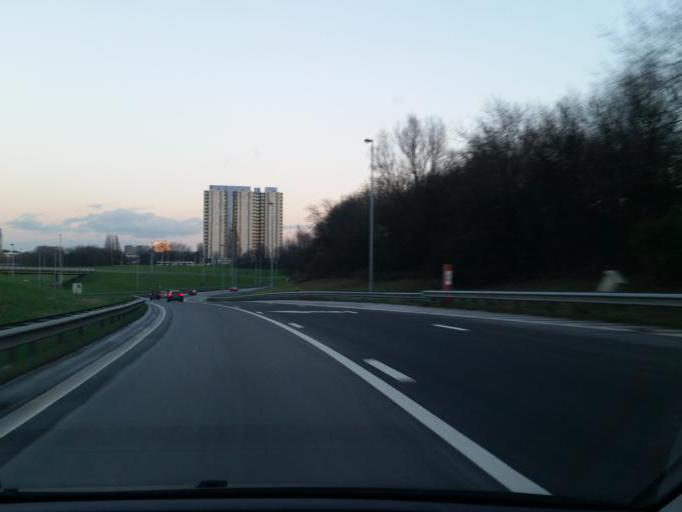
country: BE
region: Flanders
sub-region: Provincie Antwerpen
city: Antwerpen
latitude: 51.1967
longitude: 4.3804
